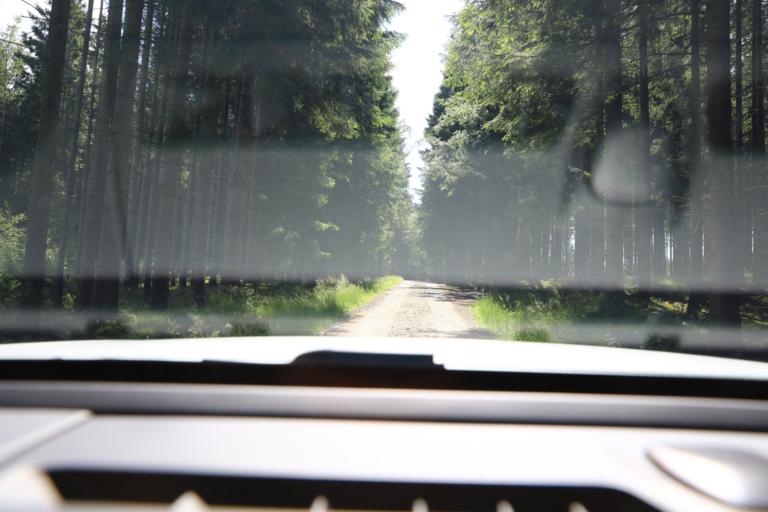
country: SE
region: Halland
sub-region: Varbergs Kommun
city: Tvaaker
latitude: 57.0994
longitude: 12.4818
